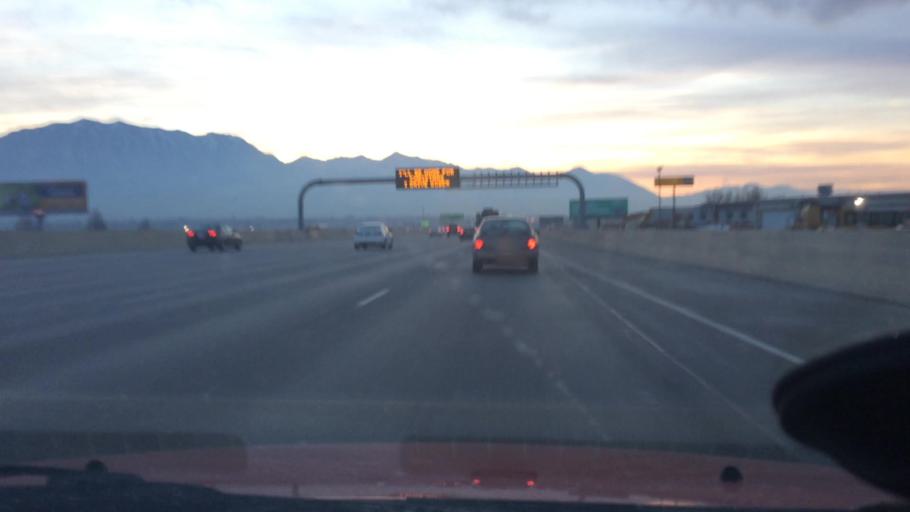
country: US
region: Utah
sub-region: Utah County
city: Pleasant Grove
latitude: 40.3424
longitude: -111.7577
